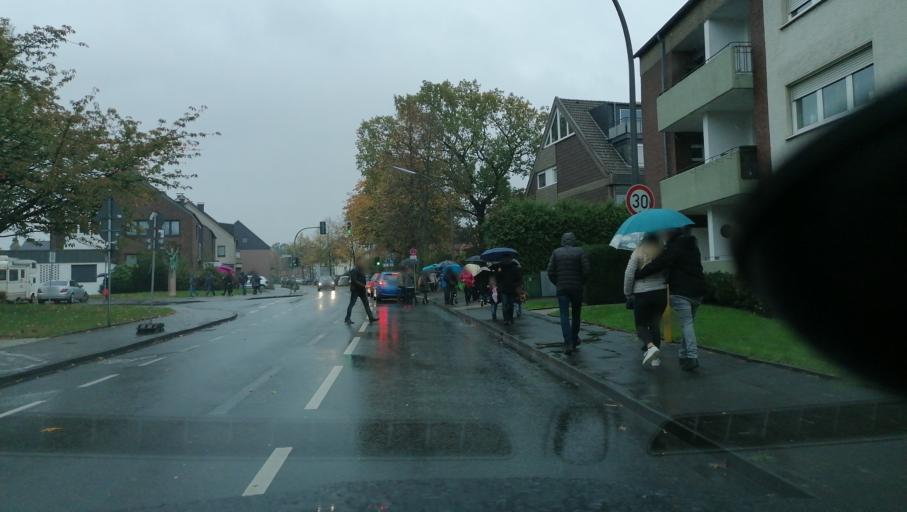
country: DE
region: North Rhine-Westphalia
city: Herten
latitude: 51.6078
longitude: 7.1696
